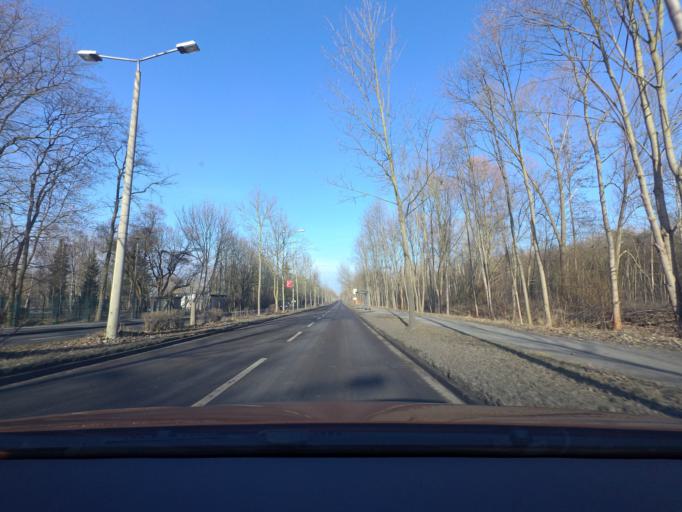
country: DE
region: Berlin
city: Blankenfelde
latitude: 52.6077
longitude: 13.3993
